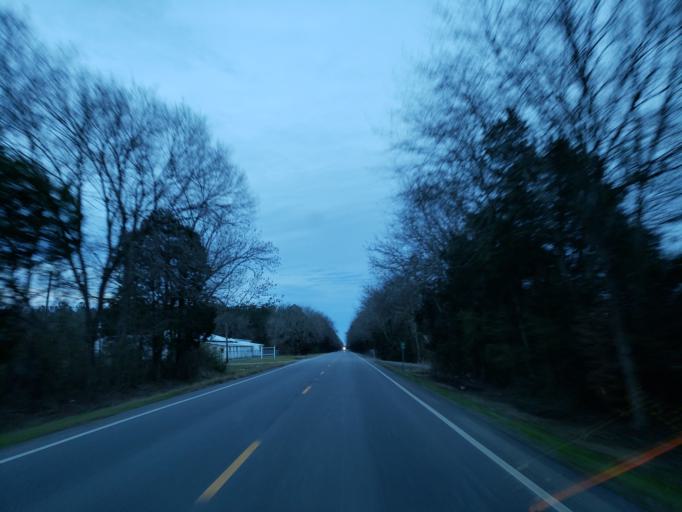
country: US
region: Alabama
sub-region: Sumter County
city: Livingston
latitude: 32.8112
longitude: -88.2447
